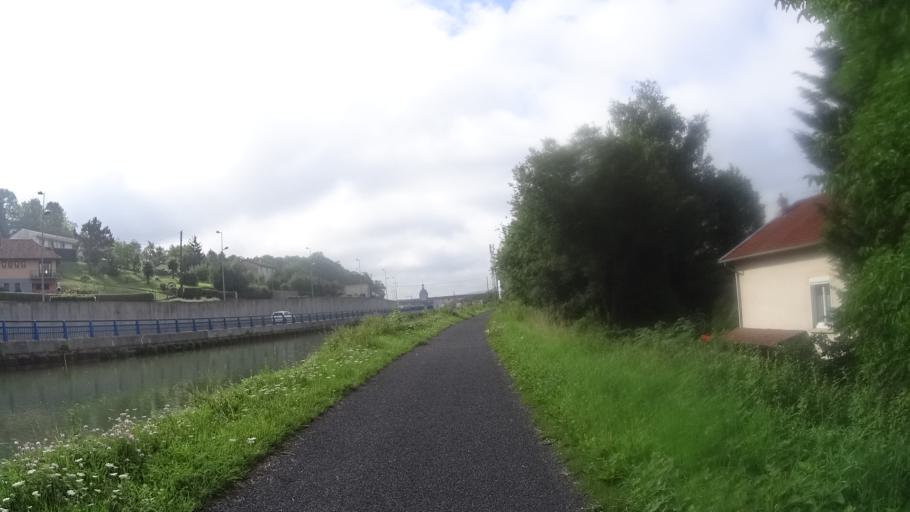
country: FR
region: Lorraine
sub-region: Departement de la Meuse
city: Bar-le-Duc
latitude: 48.7835
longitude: 5.1538
